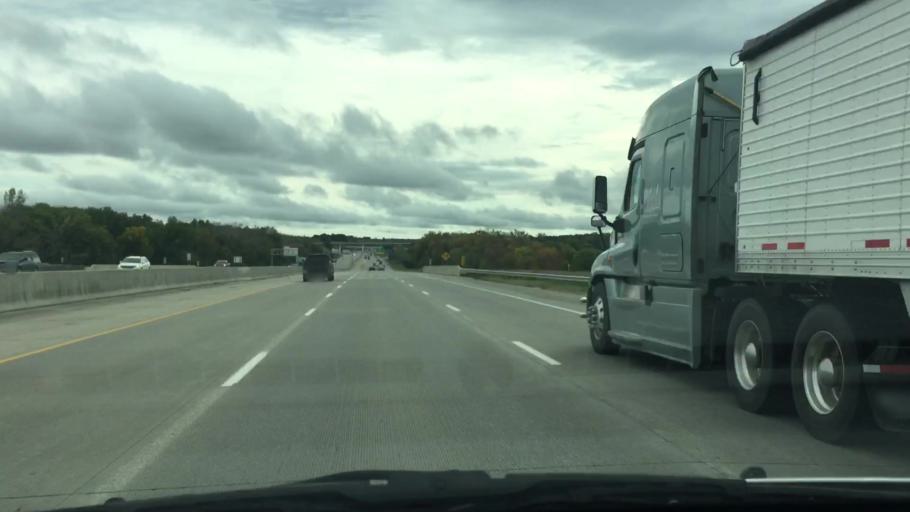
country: US
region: Iowa
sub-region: Polk County
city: West Des Moines
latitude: 41.5396
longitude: -93.7752
